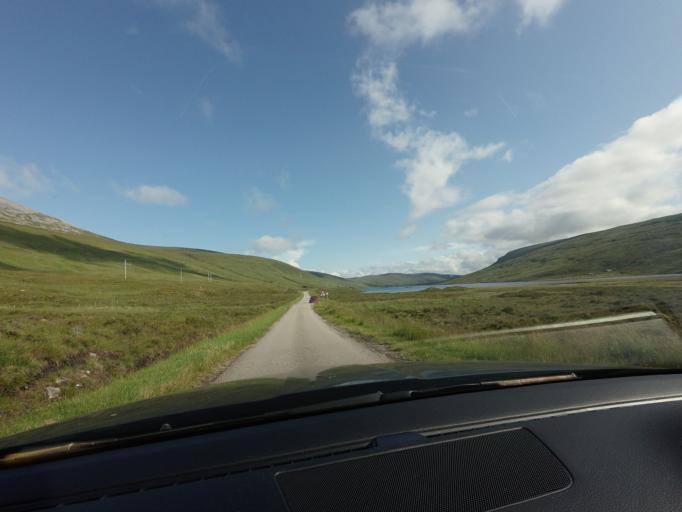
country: GB
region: Scotland
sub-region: Highland
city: Ullapool
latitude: 58.2549
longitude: -4.7541
